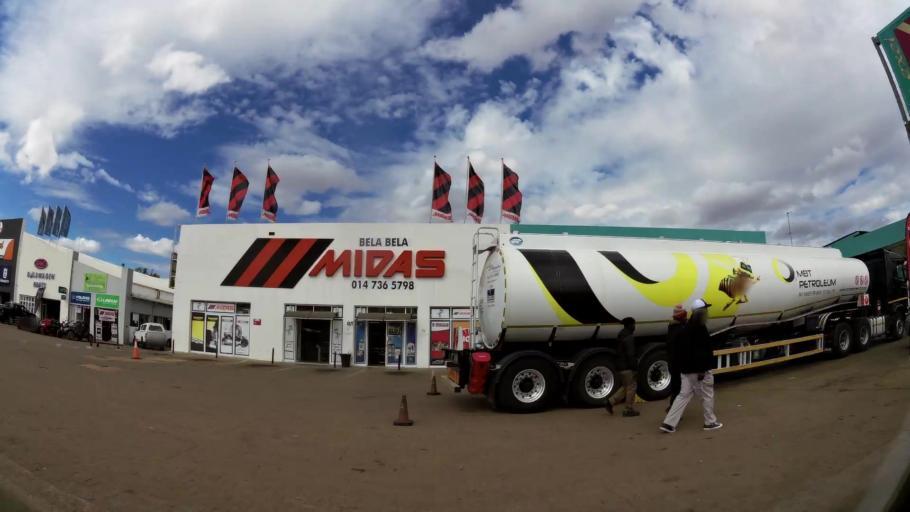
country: ZA
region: Limpopo
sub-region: Waterberg District Municipality
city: Bela-Bela
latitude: -24.8865
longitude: 28.2962
